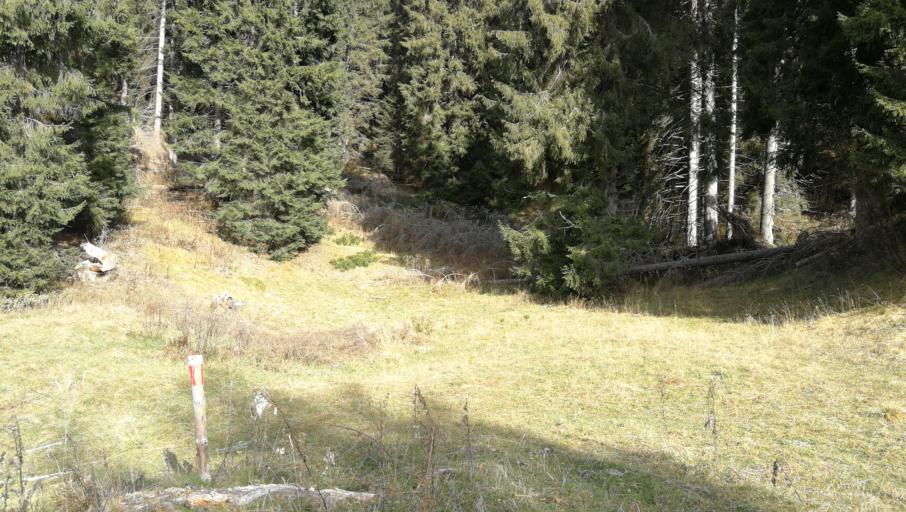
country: IT
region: Trentino-Alto Adige
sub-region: Provincia di Trento
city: Prezzo
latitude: 45.9095
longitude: 10.6479
